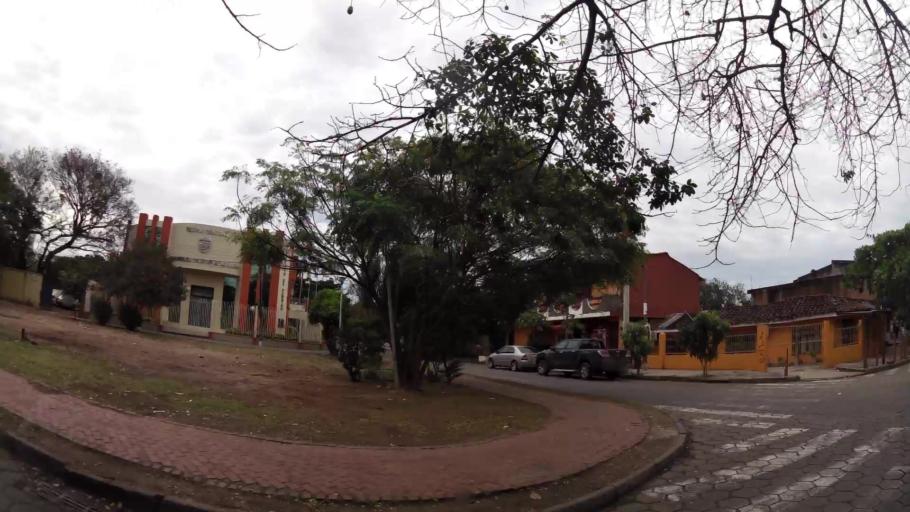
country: BO
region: Santa Cruz
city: Santa Cruz de la Sierra
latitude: -17.7753
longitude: -63.1727
